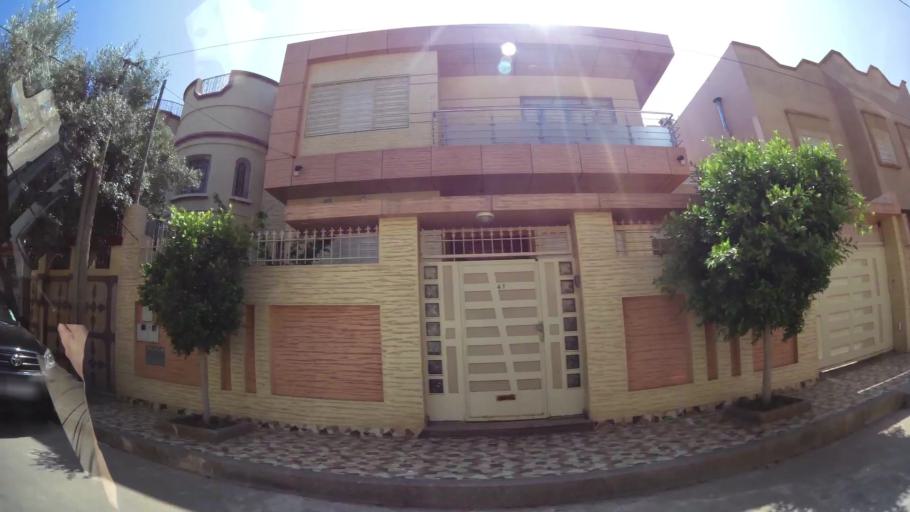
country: MA
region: Oriental
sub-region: Oujda-Angad
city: Oujda
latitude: 34.6875
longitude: -1.8751
